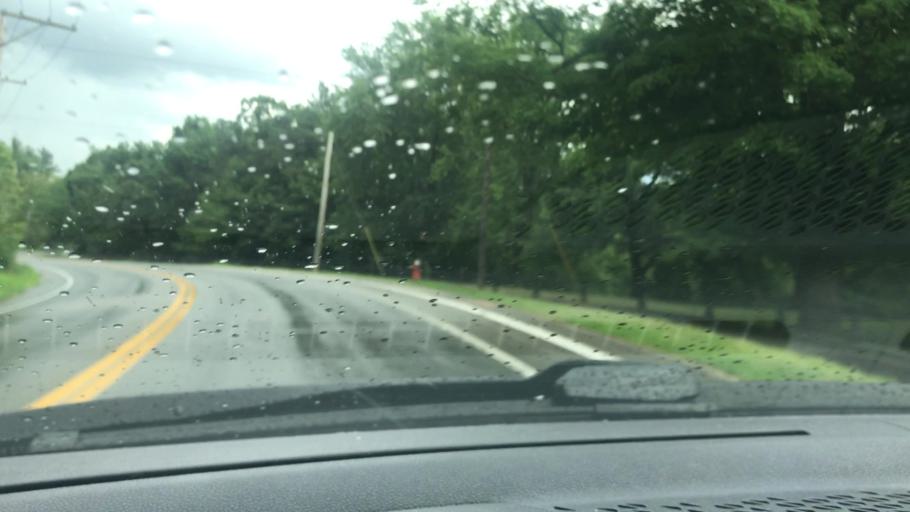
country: US
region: New Hampshire
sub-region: Merrimack County
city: Concord
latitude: 43.1962
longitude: -71.5583
